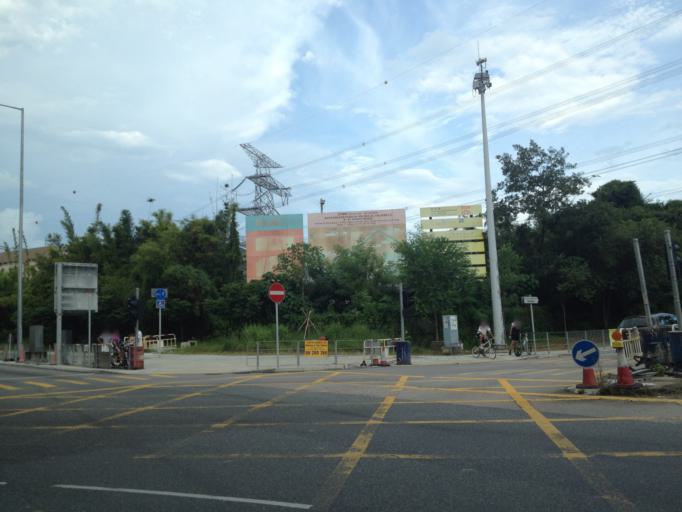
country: HK
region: Tai Po
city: Tai Po
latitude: 22.4626
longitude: 114.1487
